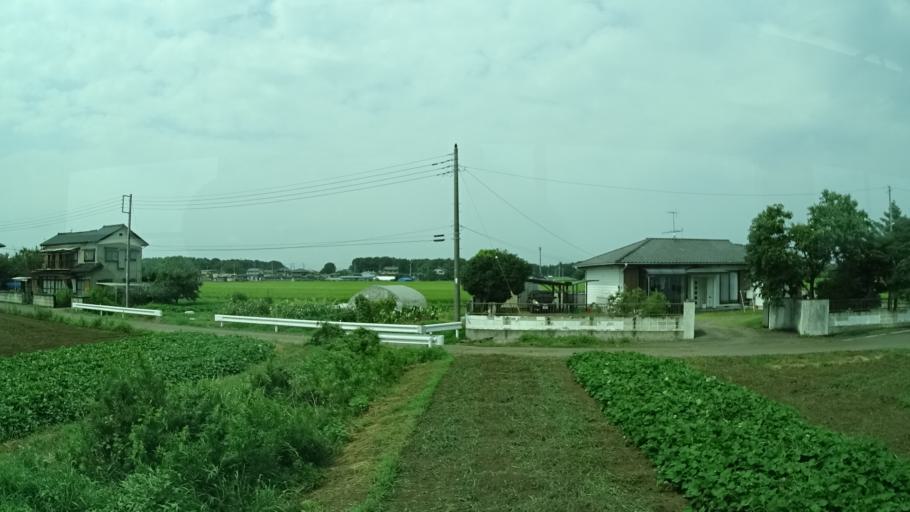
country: JP
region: Tochigi
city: Mooka
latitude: 36.4536
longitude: 140.0503
